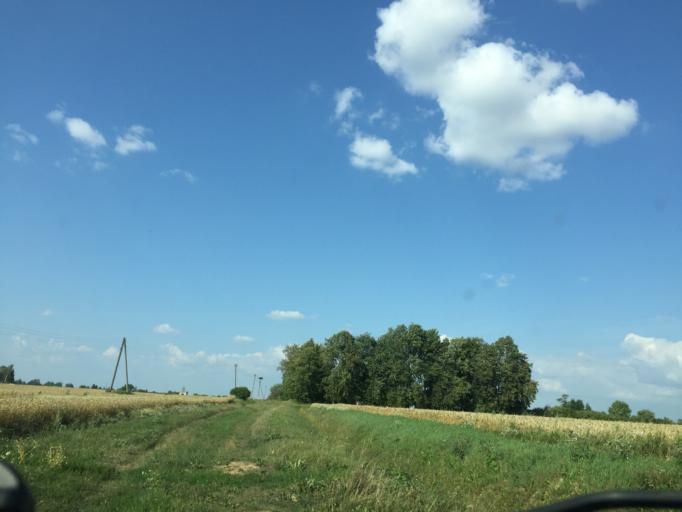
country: LV
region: Jelgava
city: Jelgava
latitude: 56.4724
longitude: 23.7055
